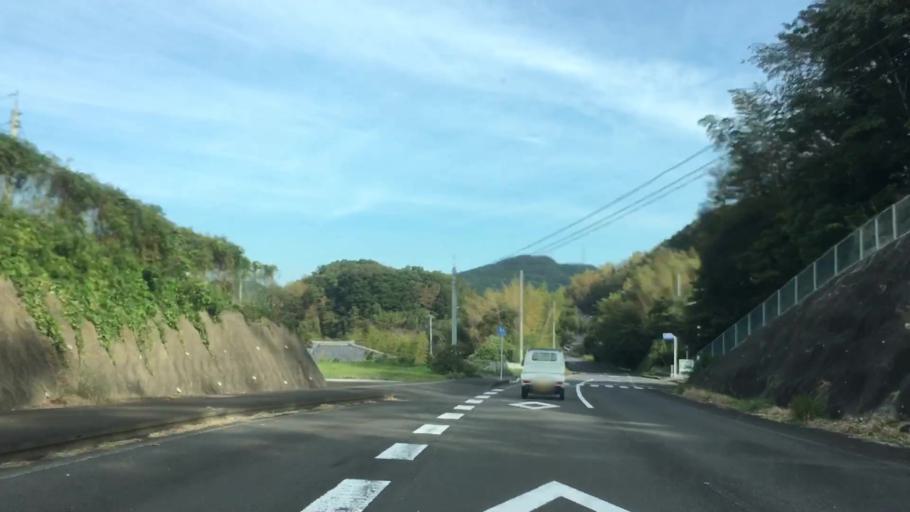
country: JP
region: Nagasaki
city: Sasebo
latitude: 33.0165
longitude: 129.6542
